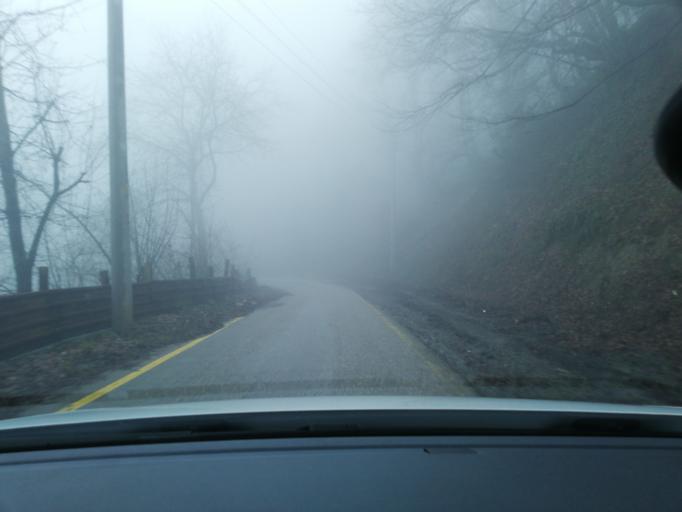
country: TR
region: Duzce
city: Kaynasli
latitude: 40.7532
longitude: 31.3780
